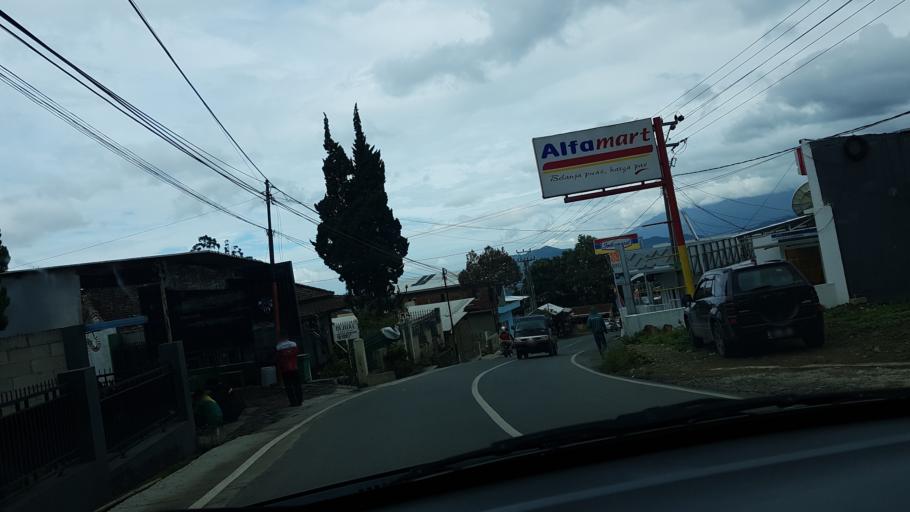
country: ID
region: West Java
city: Banjar
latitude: -7.1216
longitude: 107.4252
